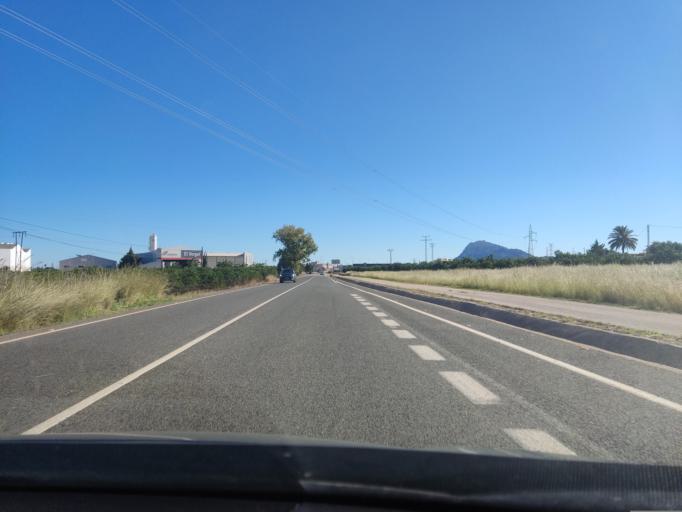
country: ES
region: Valencia
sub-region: Provincia de Alicante
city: Vergel
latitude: 38.8534
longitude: -0.0025
